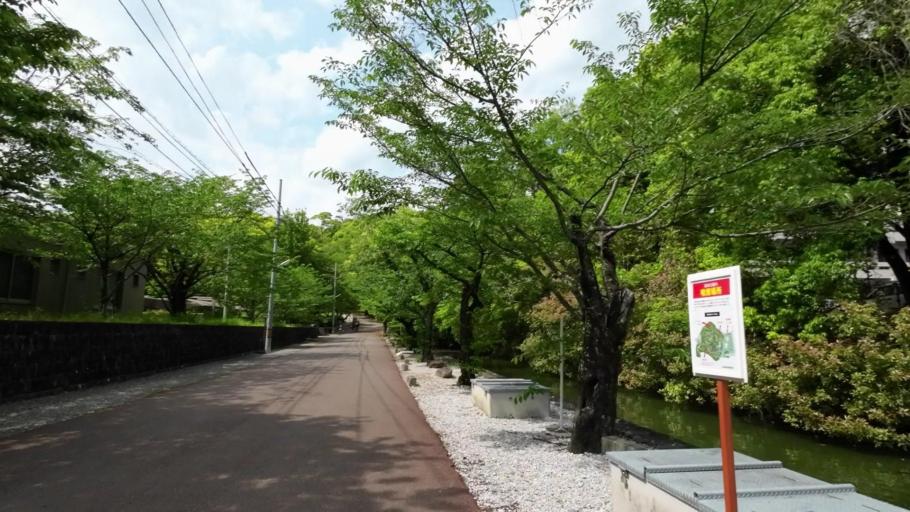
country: JP
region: Kochi
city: Kochi-shi
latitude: 33.5591
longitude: 133.5301
